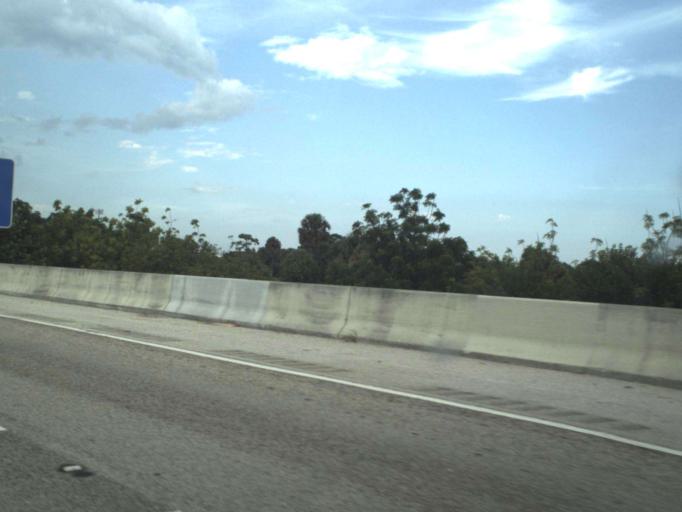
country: US
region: Florida
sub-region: Palm Beach County
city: Lake Clarke Shores
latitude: 26.6493
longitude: -80.0681
